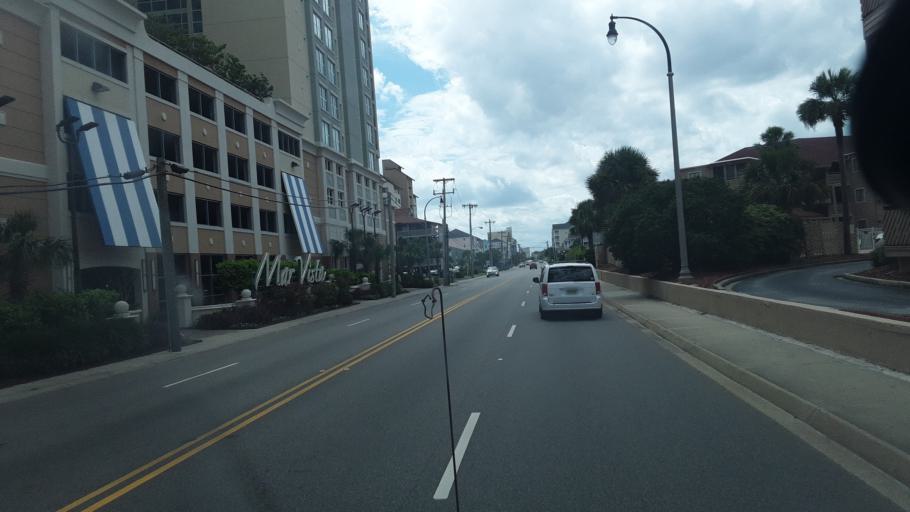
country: US
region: South Carolina
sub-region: Horry County
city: North Myrtle Beach
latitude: 33.8159
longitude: -78.6802
